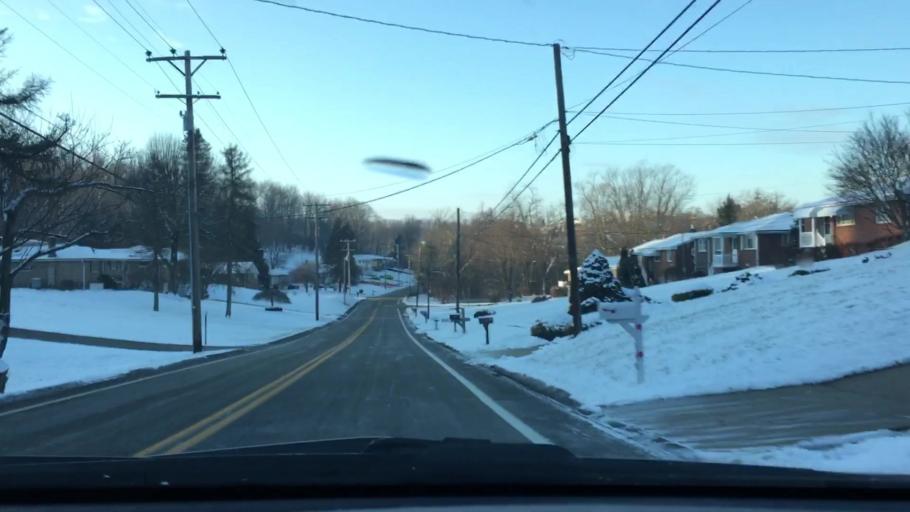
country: US
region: Pennsylvania
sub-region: Allegheny County
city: Elizabeth
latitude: 40.2678
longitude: -79.8495
